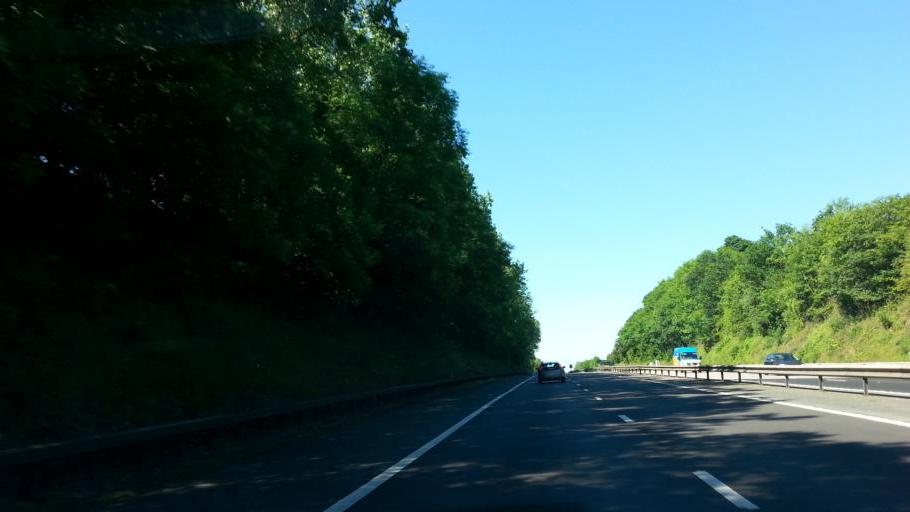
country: GB
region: England
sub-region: Herefordshire
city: Linton
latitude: 51.9320
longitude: -2.4886
